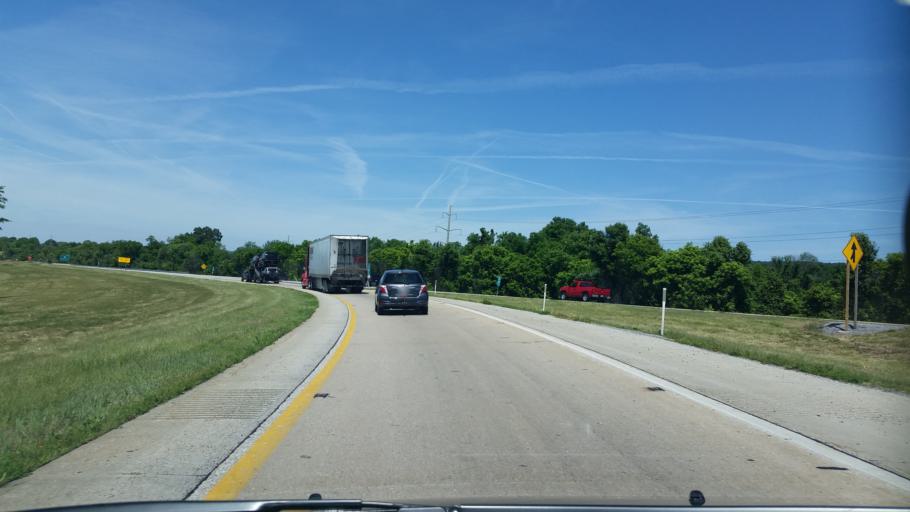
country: US
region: Pennsylvania
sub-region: Cumberland County
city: Mechanicsburg
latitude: 40.2750
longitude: -77.0020
